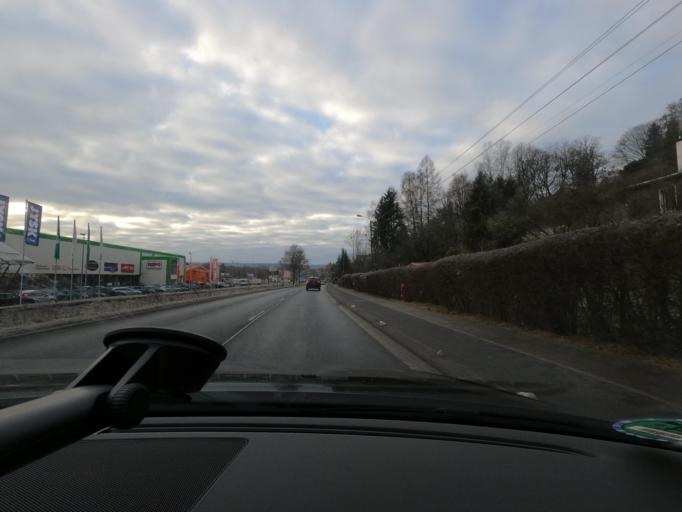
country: DE
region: Thuringia
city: Schleusingen
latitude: 50.5172
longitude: 10.7538
